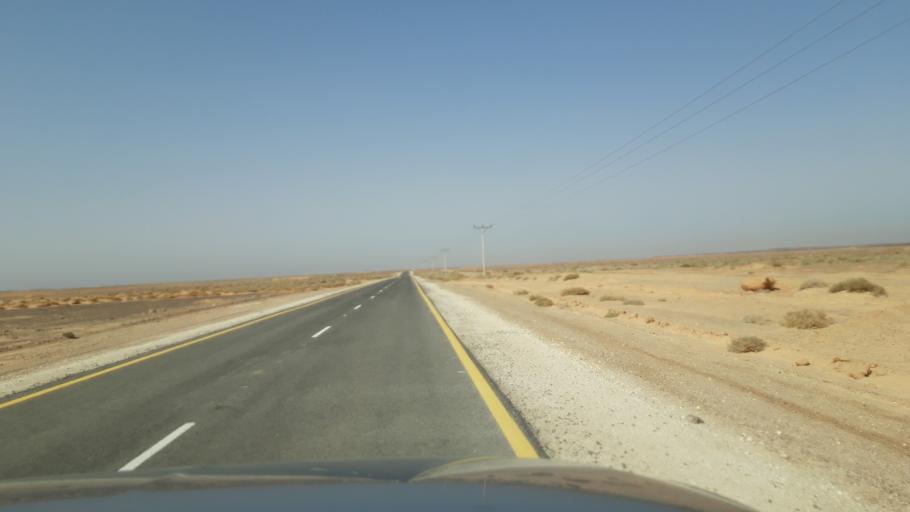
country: JO
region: Amman
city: Al Azraq ash Shamali
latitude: 31.7786
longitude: 36.7803
